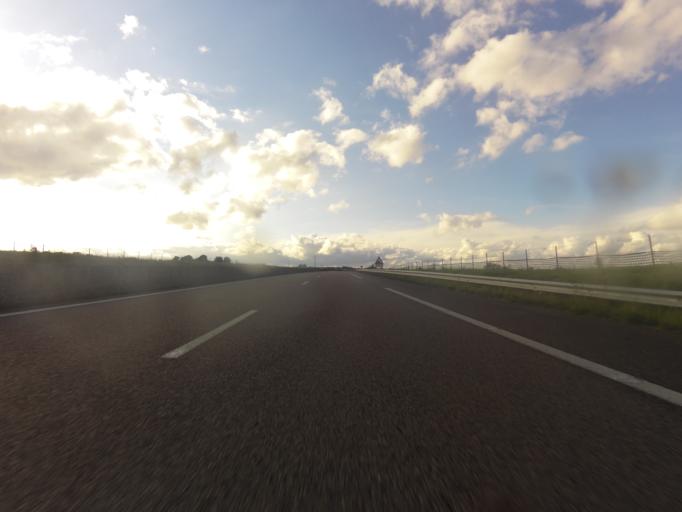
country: FR
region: Haute-Normandie
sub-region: Departement de la Seine-Maritime
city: Gaillefontaine
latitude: 49.7358
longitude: 1.5520
